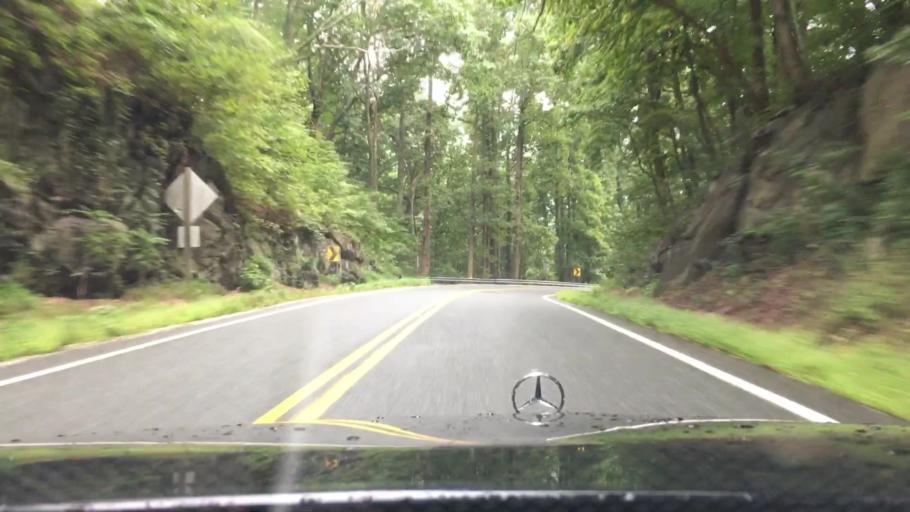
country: US
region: Virginia
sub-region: Nelson County
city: Nellysford
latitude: 37.8518
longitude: -78.9226
